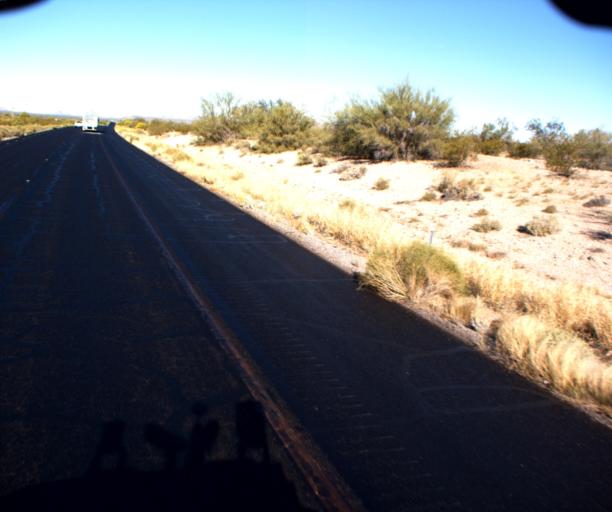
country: US
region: Arizona
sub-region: Pinal County
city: Maricopa
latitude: 32.8368
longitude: -112.2091
